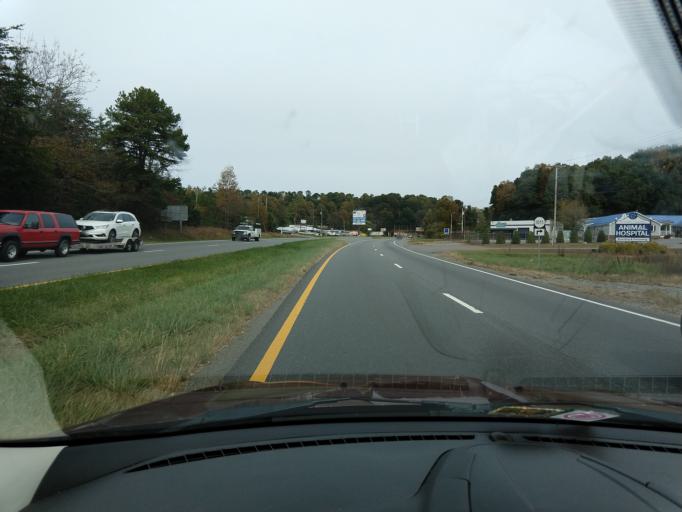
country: US
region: Virginia
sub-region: Franklin County
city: Rocky Mount
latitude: 37.0304
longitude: -79.8793
